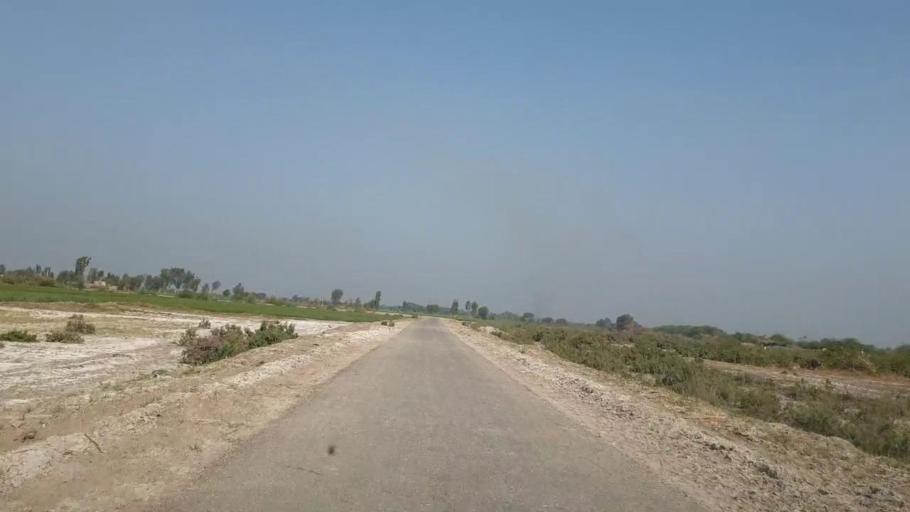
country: PK
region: Sindh
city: Mirpur Khas
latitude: 25.5826
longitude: 69.0049
